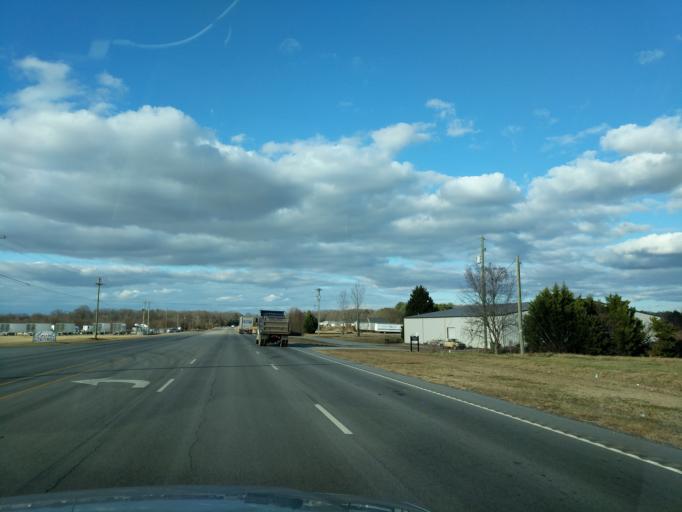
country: US
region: South Carolina
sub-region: Greenville County
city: Five Forks
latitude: 34.8403
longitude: -82.1461
